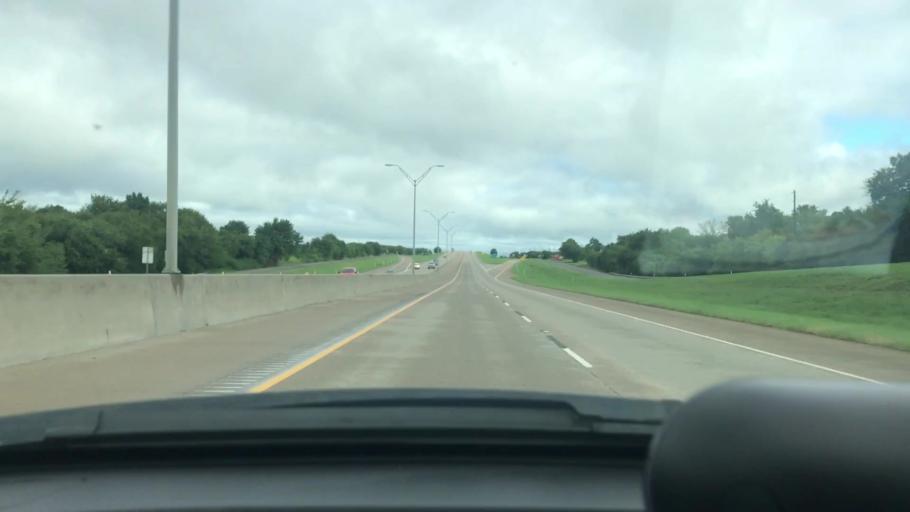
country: US
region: Texas
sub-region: Grayson County
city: Van Alstyne
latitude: 33.4573
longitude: -96.6084
